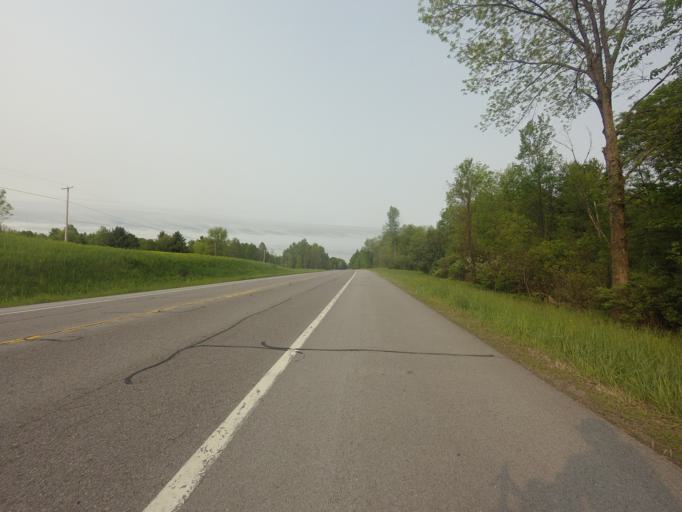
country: US
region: New York
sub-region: Jefferson County
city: Carthage
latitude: 44.0589
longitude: -75.5424
